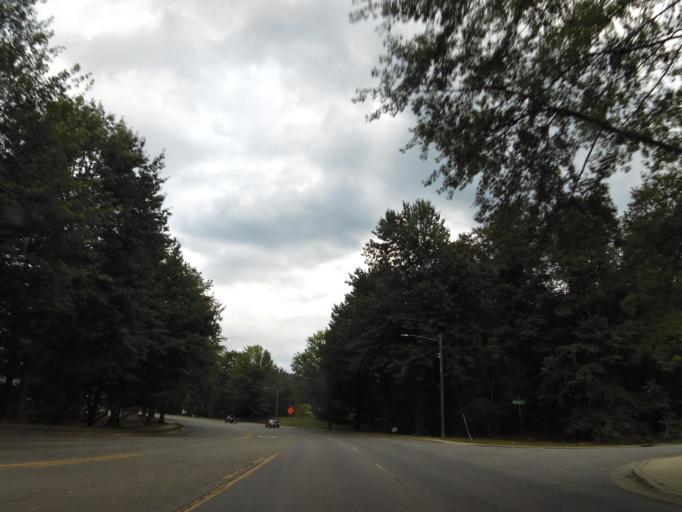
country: US
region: North Carolina
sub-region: Buncombe County
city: Asheville
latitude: 35.5953
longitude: -82.5465
